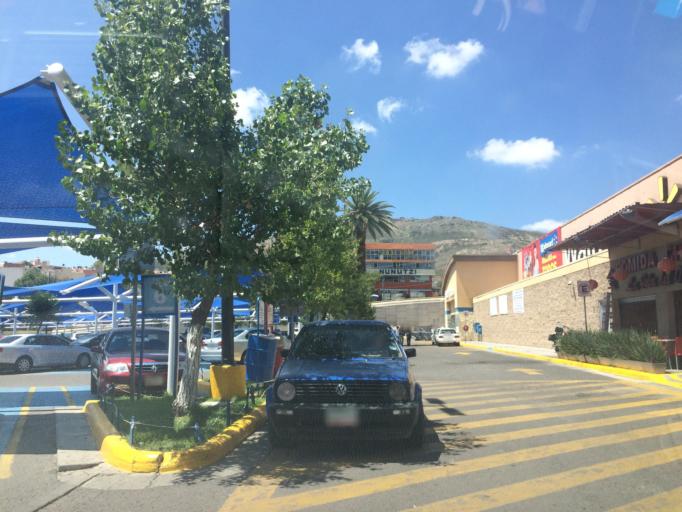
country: MX
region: Zacatecas
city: Zacatecas
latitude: 22.7625
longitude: -102.5503
